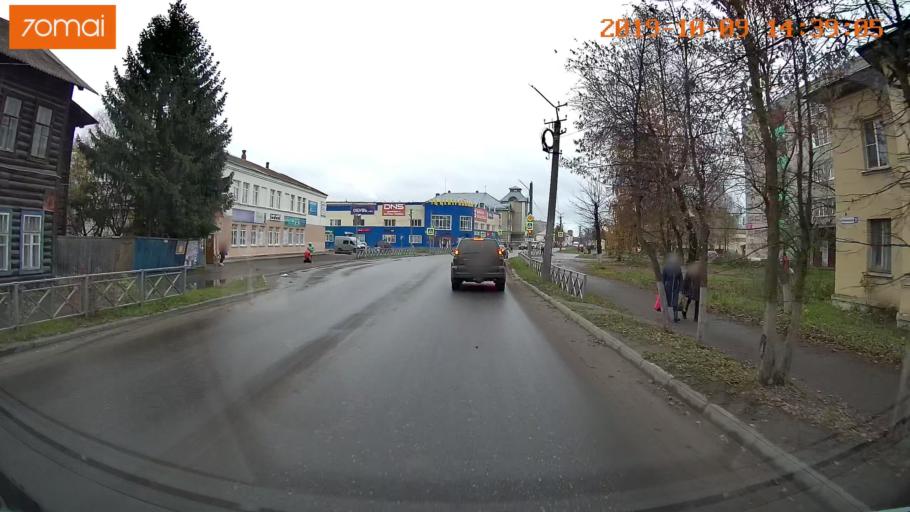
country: RU
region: Kostroma
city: Buy
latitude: 58.4772
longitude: 41.5385
